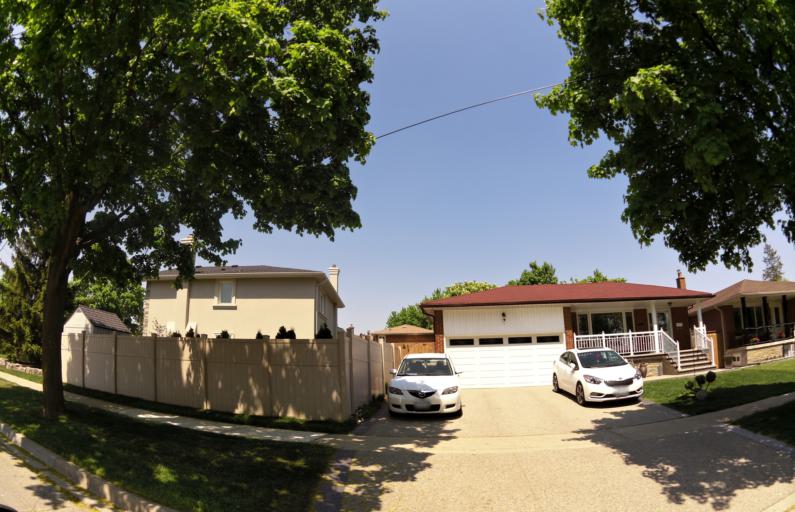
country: CA
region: Ontario
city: Mississauga
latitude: 43.6027
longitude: -79.6179
